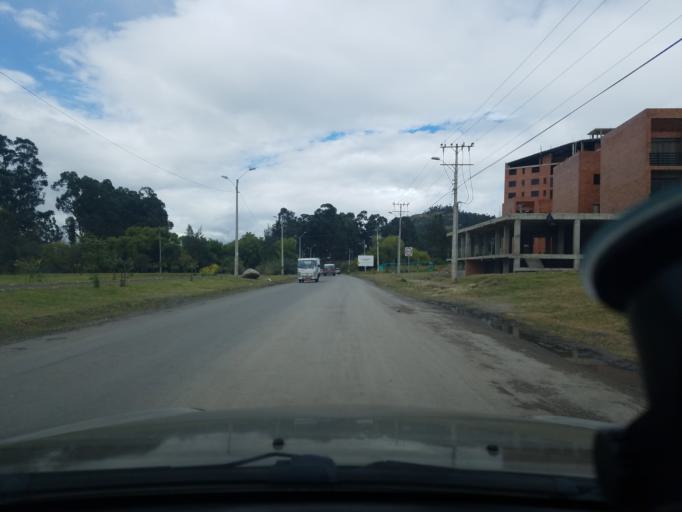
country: EC
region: Azuay
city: Cuenca
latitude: -2.8962
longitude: -78.9687
